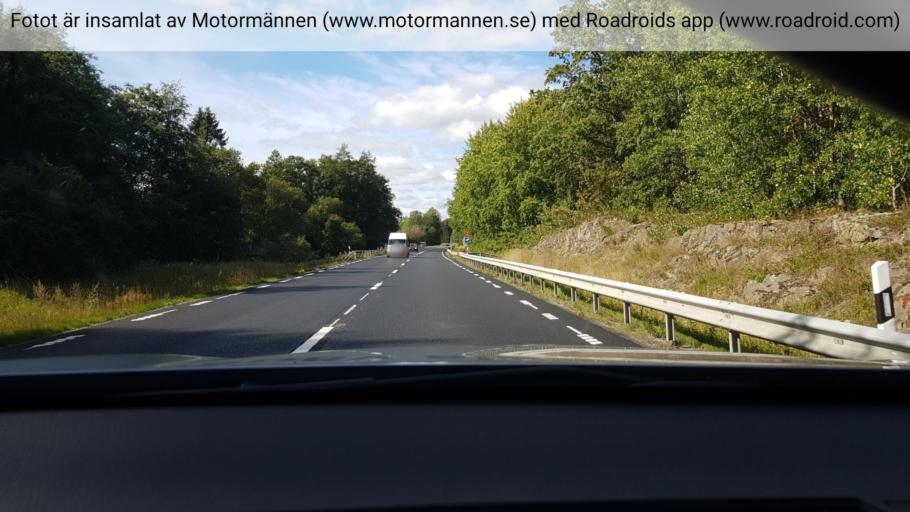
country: SE
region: Stockholm
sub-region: Osterakers Kommun
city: Akersberga
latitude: 59.4263
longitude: 18.2693
